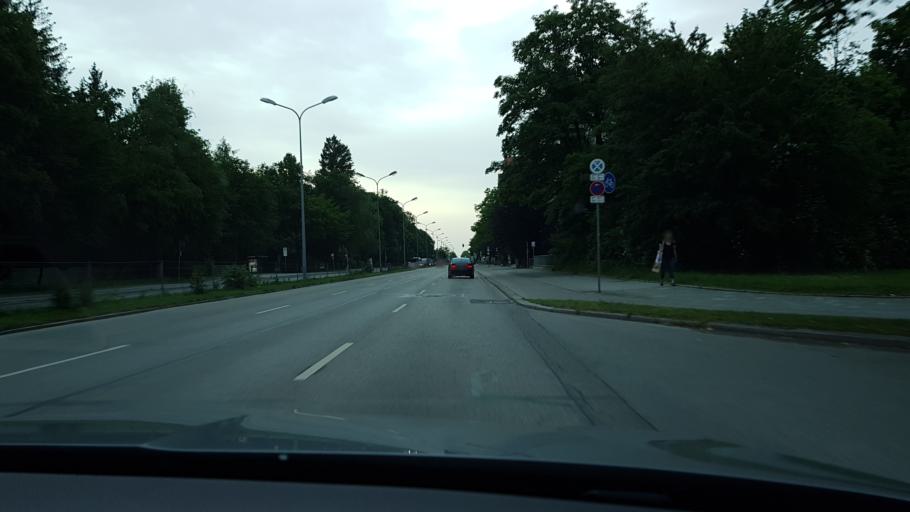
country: DE
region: Bavaria
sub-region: Upper Bavaria
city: Neuried
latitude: 48.1071
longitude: 11.5022
